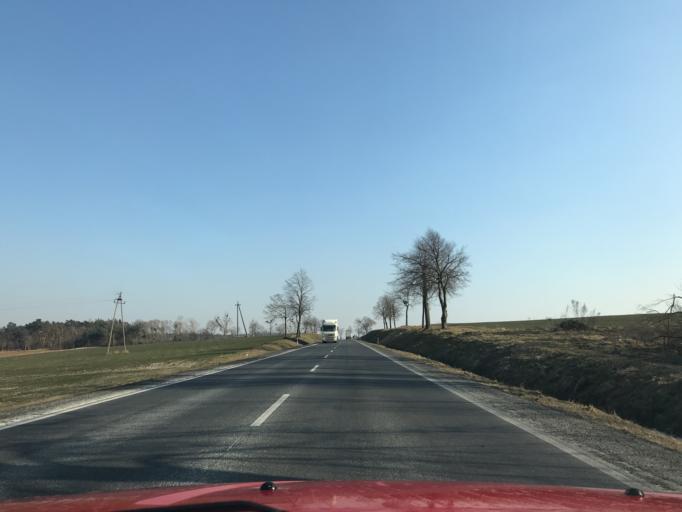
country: PL
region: Greater Poland Voivodeship
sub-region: Powiat sredzki
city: Nowe Miasto nad Warta
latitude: 52.0817
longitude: 17.4080
